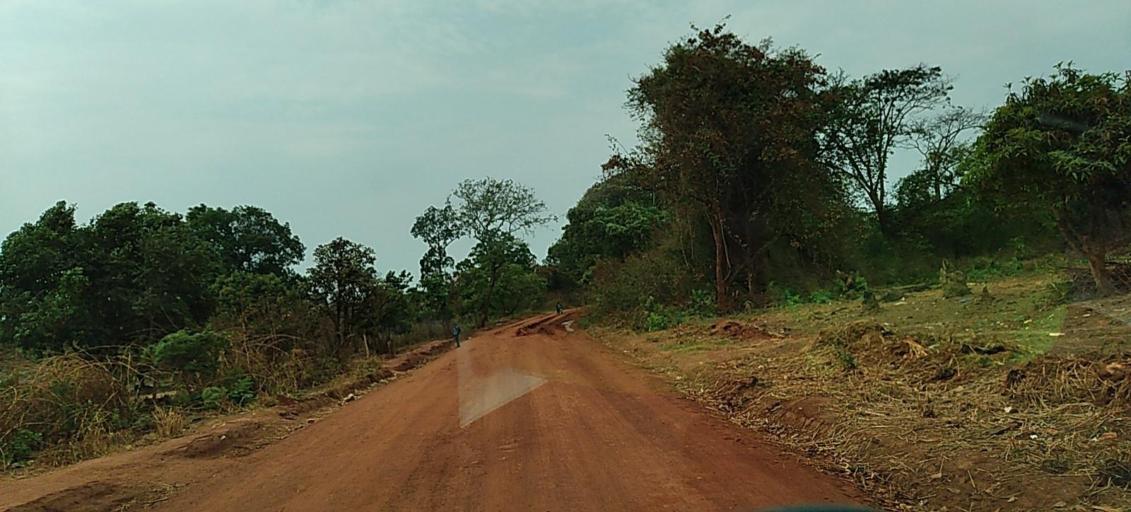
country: ZM
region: North-Western
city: Solwezi
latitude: -12.2453
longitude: 26.5124
